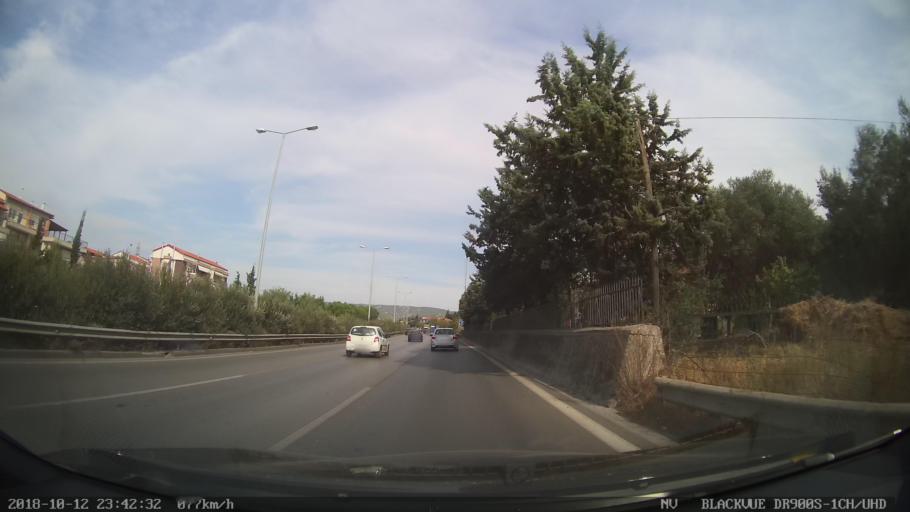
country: GR
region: Central Macedonia
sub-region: Nomos Thessalonikis
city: Pylaia
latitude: 40.5947
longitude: 22.9947
